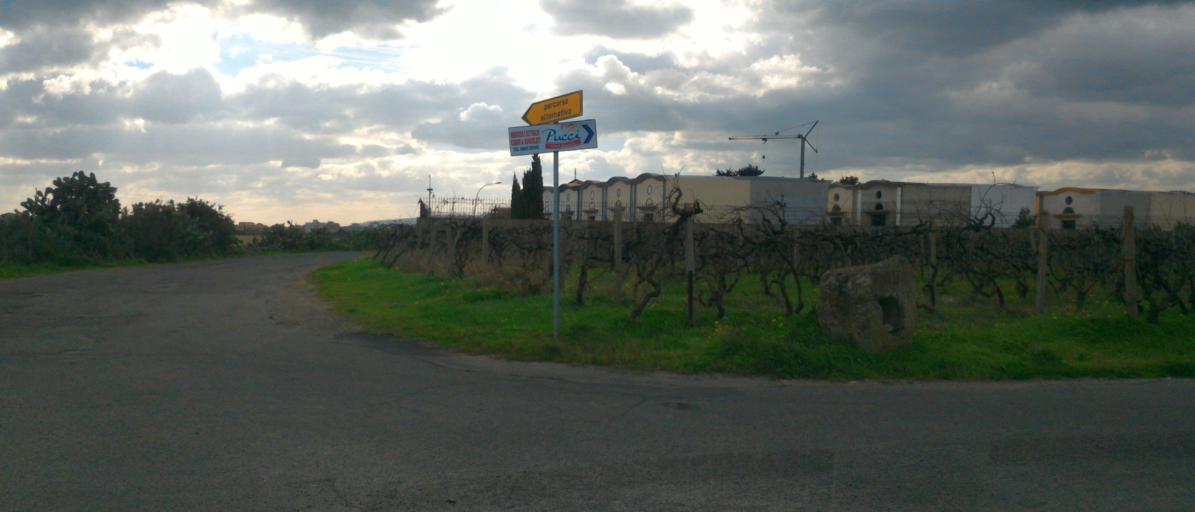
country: IT
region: Calabria
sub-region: Provincia di Crotone
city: Ciro Marina
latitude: 39.3906
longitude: 17.1390
